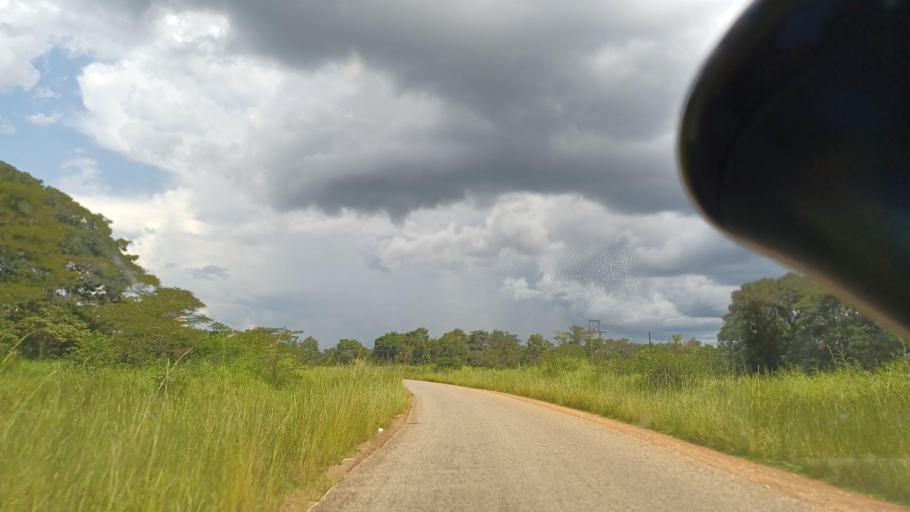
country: ZM
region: North-Western
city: Kasempa
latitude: -12.7799
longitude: 26.0089
